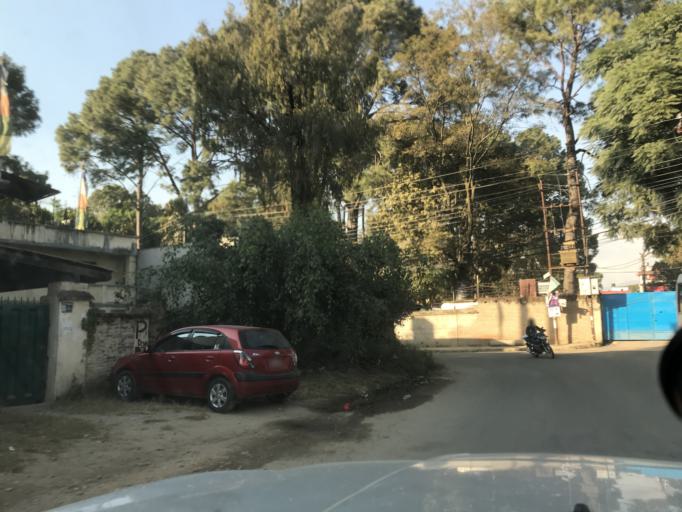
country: NP
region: Central Region
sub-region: Bagmati Zone
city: Patan
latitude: 27.6738
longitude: 85.3121
